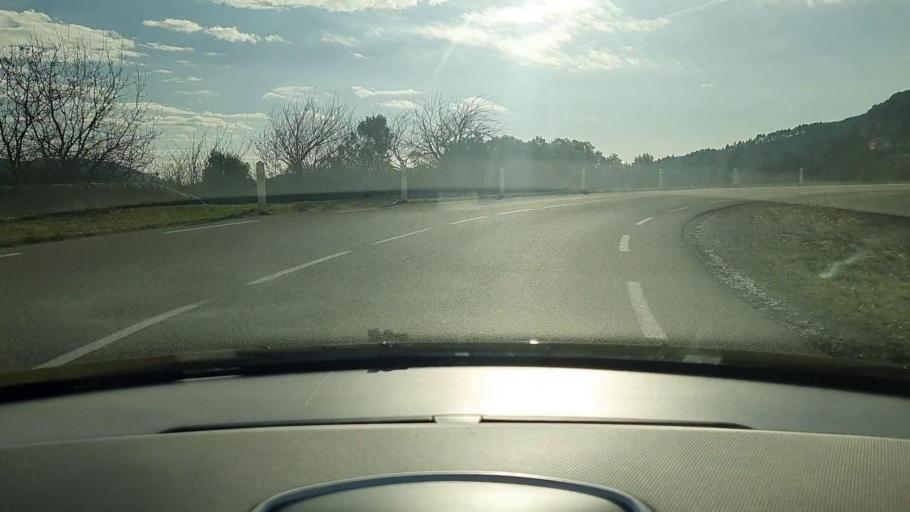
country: FR
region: Languedoc-Roussillon
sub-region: Departement du Gard
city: Branoux-les-Taillades
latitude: 44.4019
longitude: 3.9342
